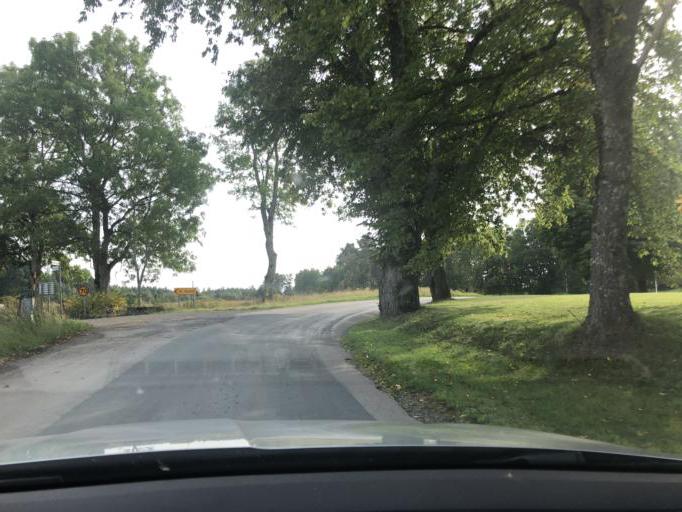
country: SE
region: Joenkoeping
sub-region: Vetlanda Kommun
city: Ekenassjon
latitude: 57.5109
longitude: 14.9068
